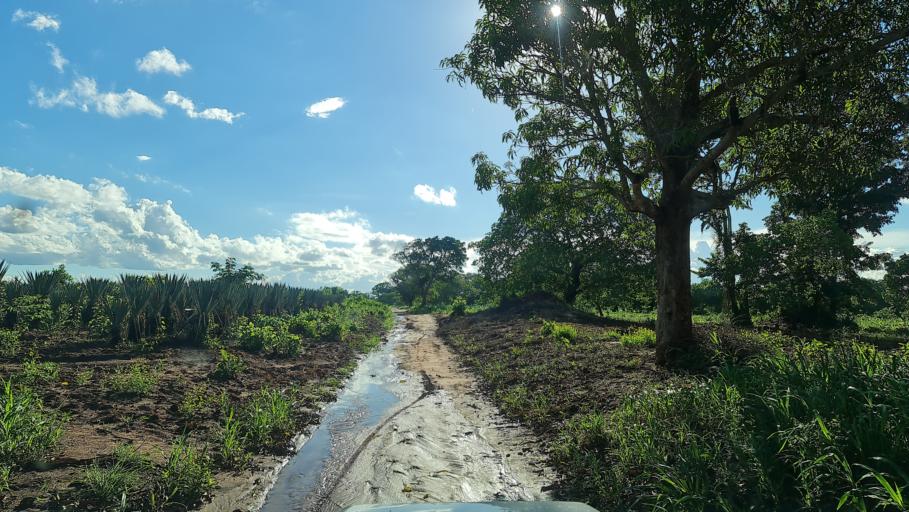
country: MZ
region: Nampula
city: Ilha de Mocambique
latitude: -14.9352
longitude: 40.2083
